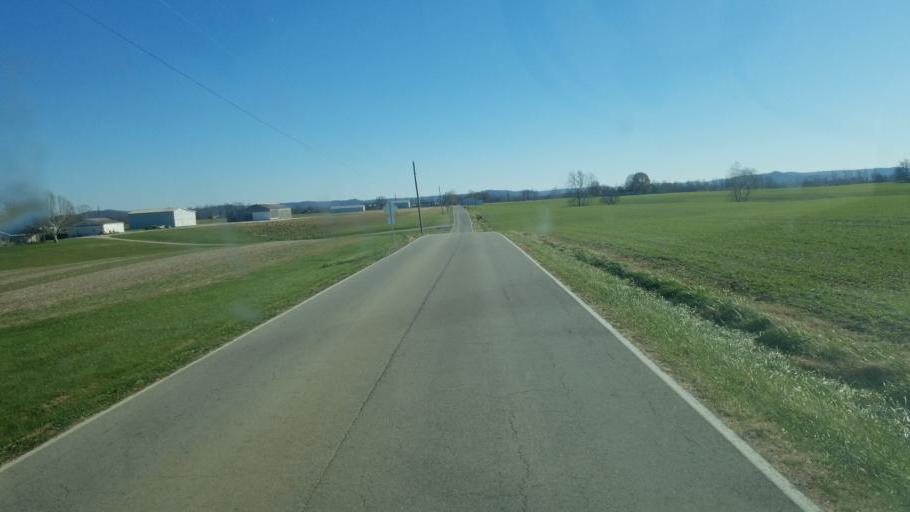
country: US
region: Kentucky
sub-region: Mason County
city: Maysville
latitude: 38.5408
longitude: -83.6345
